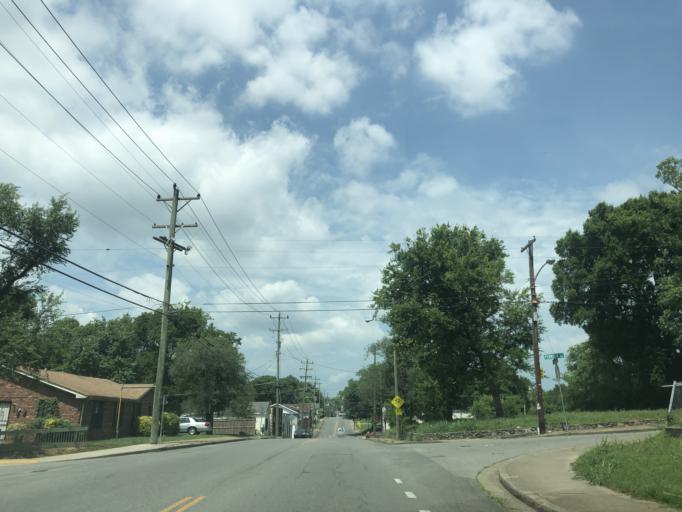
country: US
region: Tennessee
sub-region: Davidson County
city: Nashville
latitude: 36.1939
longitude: -86.7657
